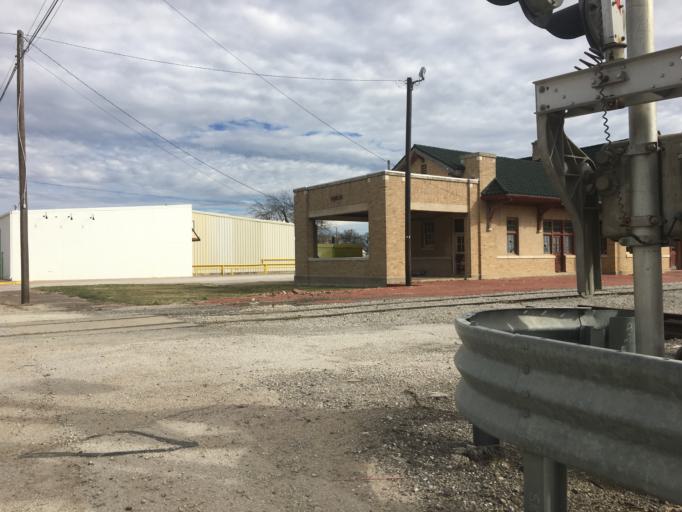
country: US
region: Texas
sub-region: Erath County
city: Dublin
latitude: 32.0832
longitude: -98.3430
